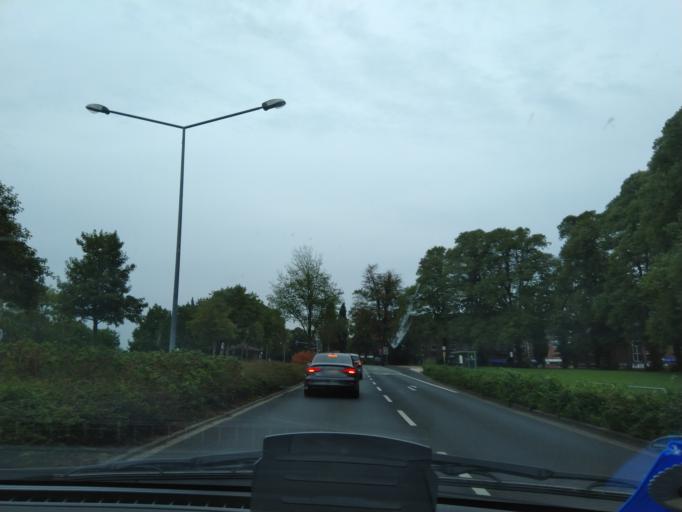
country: DE
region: Lower Saxony
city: Meppen
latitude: 52.6927
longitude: 7.2879
